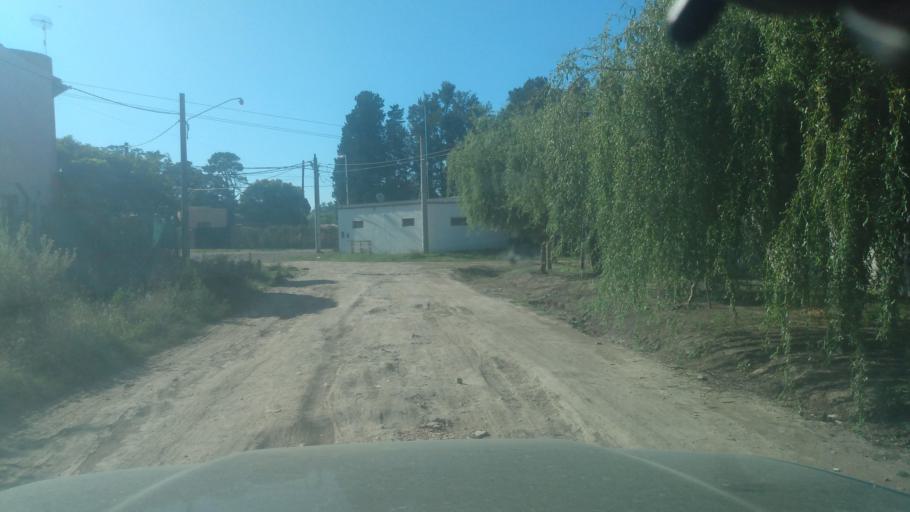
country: AR
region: Buenos Aires
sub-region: Partido de Lujan
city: Lujan
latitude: -34.5863
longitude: -59.0590
